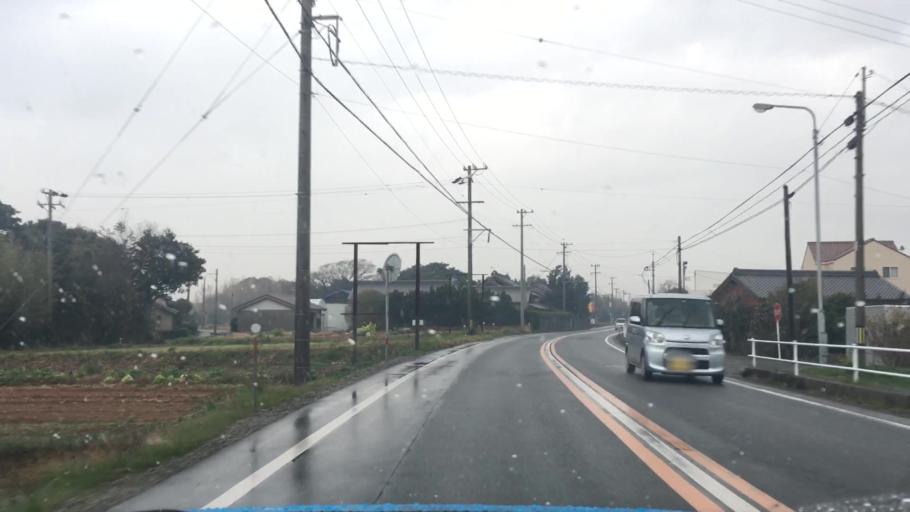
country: JP
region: Aichi
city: Tahara
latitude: 34.6612
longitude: 137.3656
